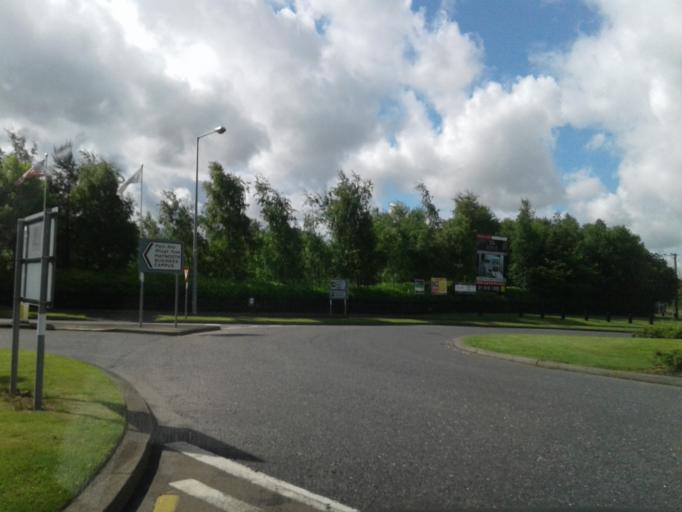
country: IE
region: Leinster
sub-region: Kildare
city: Maynooth
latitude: 53.3657
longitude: -6.5908
